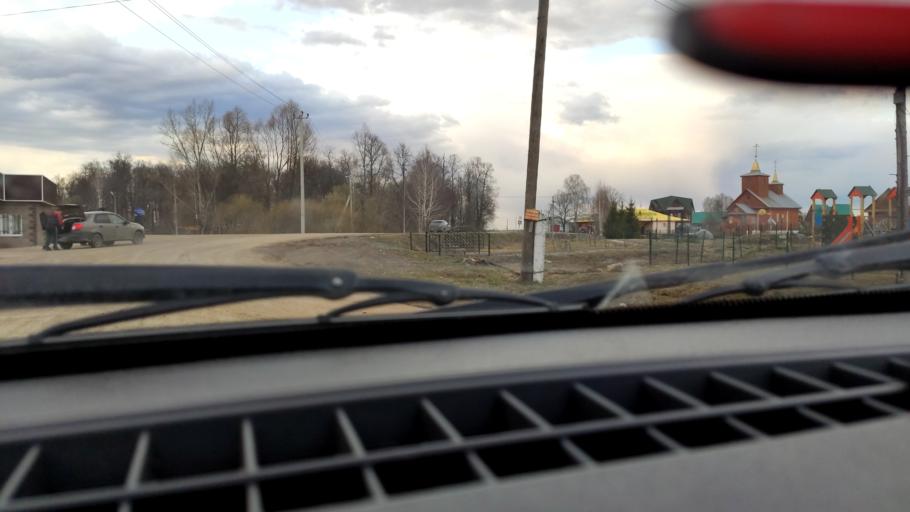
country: RU
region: Bashkortostan
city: Kudeyevskiy
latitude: 54.8125
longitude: 56.7528
